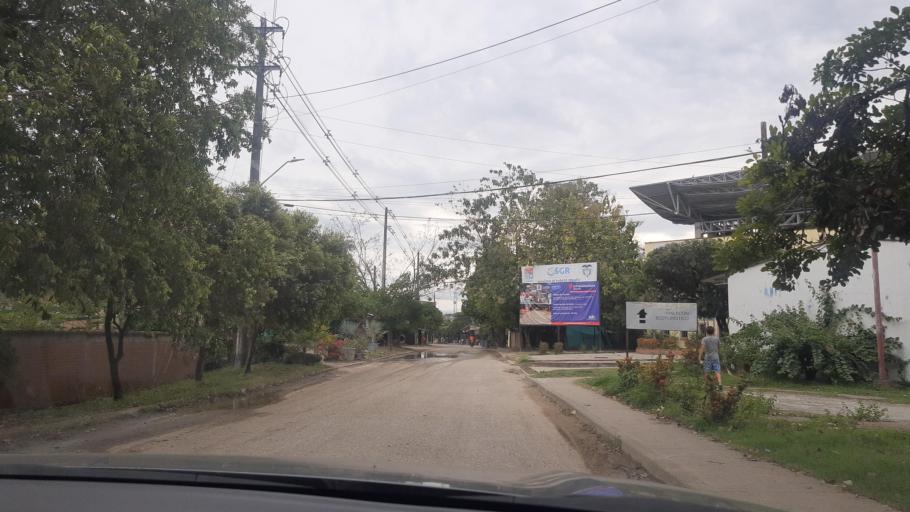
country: CO
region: Antioquia
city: Puerto Triunfo
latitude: 5.8755
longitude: -74.6377
